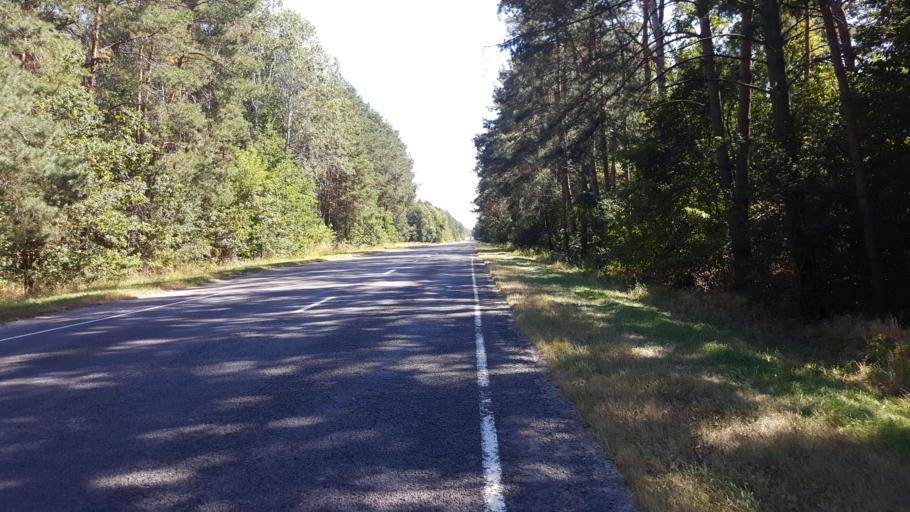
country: PL
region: Lublin Voivodeship
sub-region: Powiat bialski
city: Terespol
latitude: 52.2282
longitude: 23.5192
